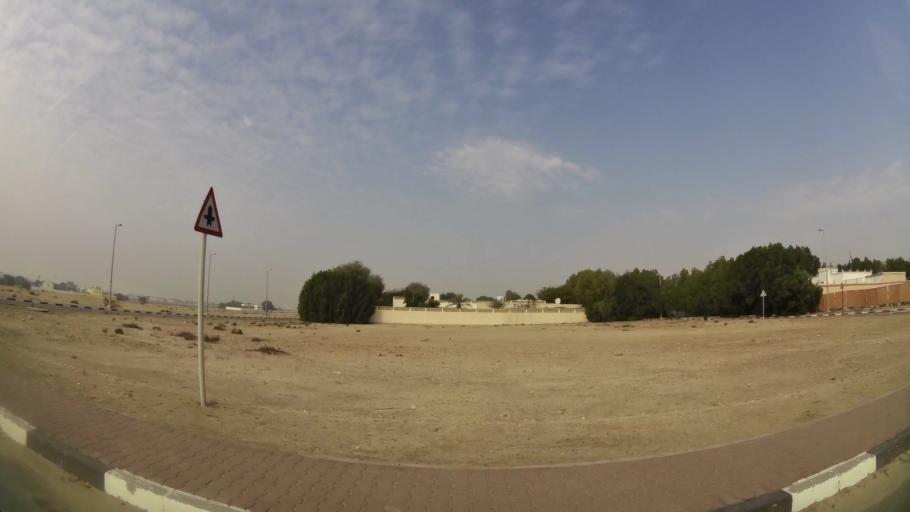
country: AE
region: Abu Dhabi
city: Abu Dhabi
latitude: 24.6785
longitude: 54.7755
